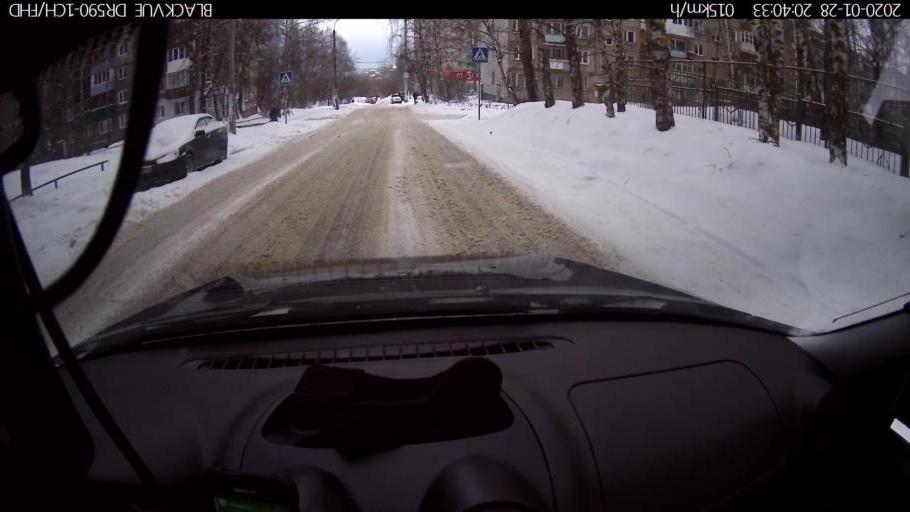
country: RU
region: Nizjnij Novgorod
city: Nizhniy Novgorod
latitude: 56.2314
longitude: 43.9545
